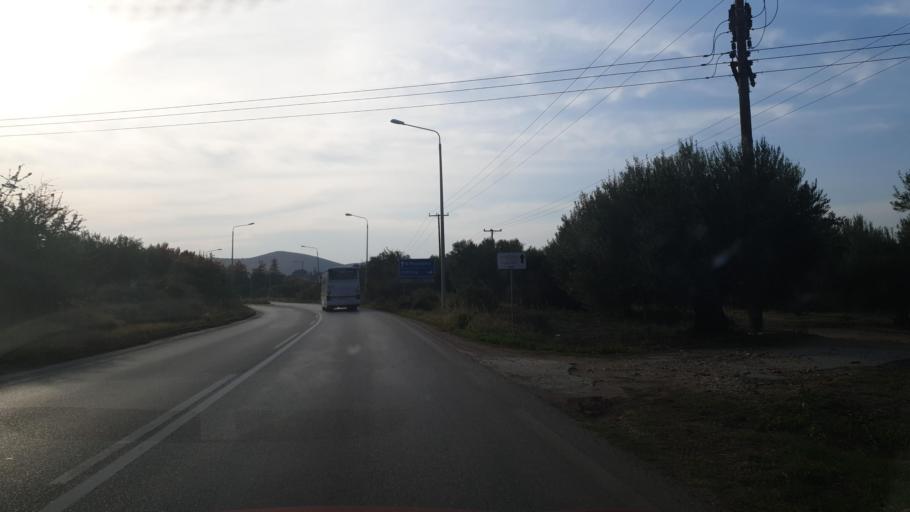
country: GR
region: Central Macedonia
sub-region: Nomos Chalkidikis
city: Ormylia
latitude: 40.2623
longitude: 23.5189
